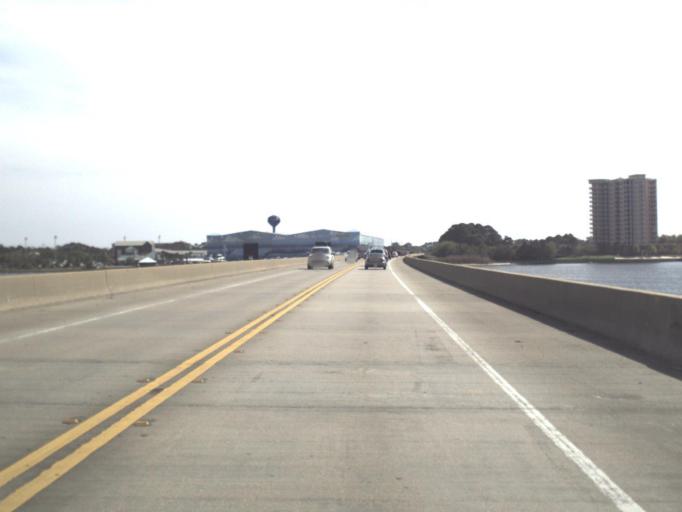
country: US
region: Florida
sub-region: Okaloosa County
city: Destin
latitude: 30.4076
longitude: -86.4241
